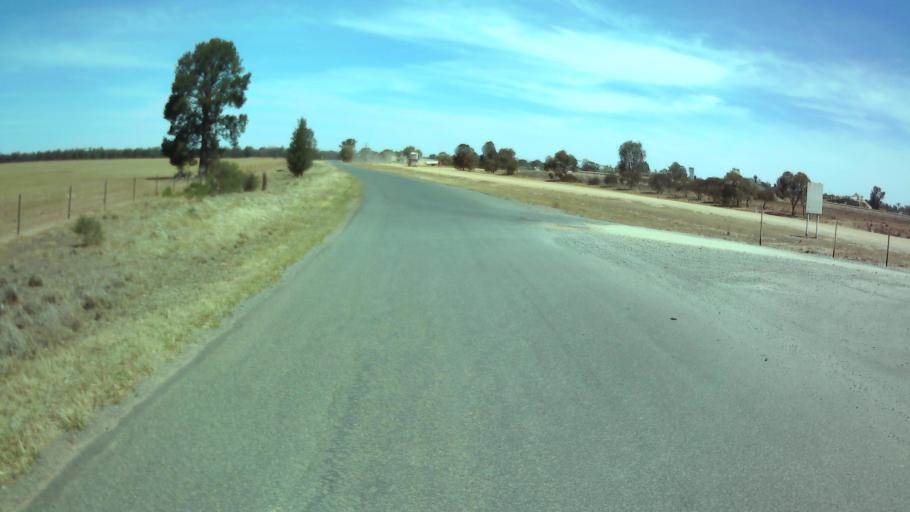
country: AU
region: New South Wales
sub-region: Weddin
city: Grenfell
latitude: -33.8318
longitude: 147.7456
